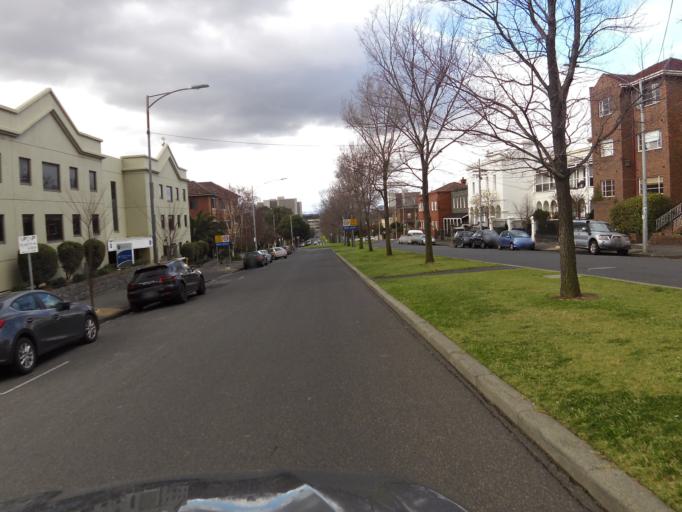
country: AU
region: Victoria
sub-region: Melbourne
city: East Melbourne
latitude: -37.8117
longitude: 144.9846
